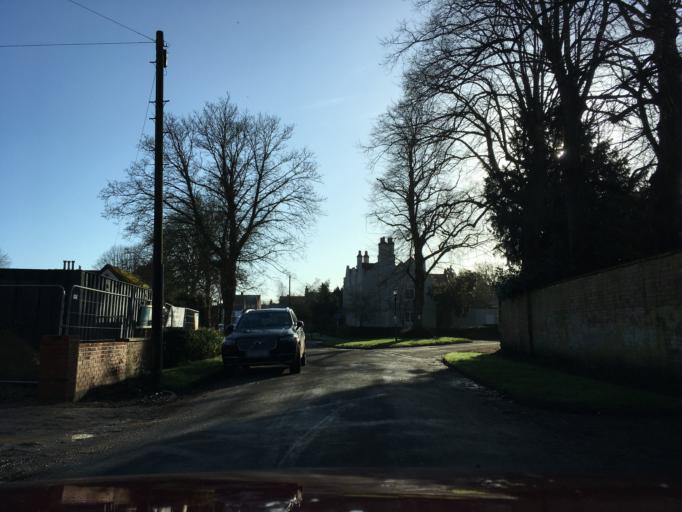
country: GB
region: England
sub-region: Warwickshire
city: Stratford-upon-Avon
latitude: 52.2075
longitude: -1.6581
